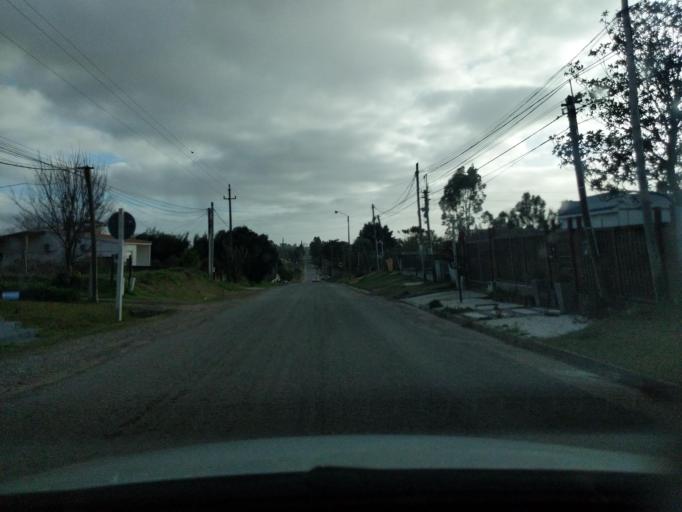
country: UY
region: Florida
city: Florida
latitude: -34.0827
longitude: -56.2124
